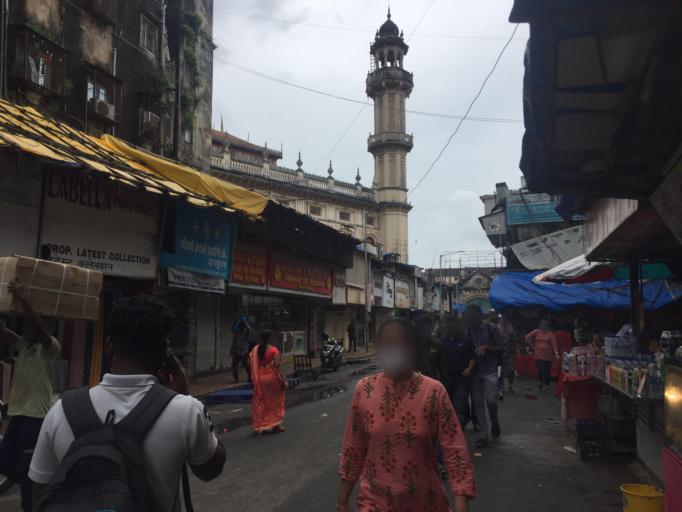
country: IN
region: Maharashtra
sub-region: Raigarh
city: Uran
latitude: 18.9498
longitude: 72.8330
